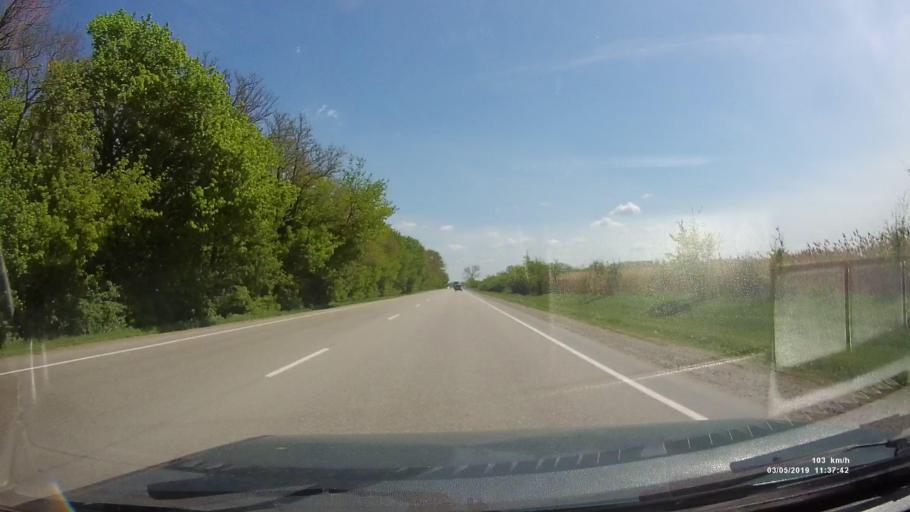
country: RU
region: Rostov
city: Ol'ginskaya
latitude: 47.1312
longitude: 39.9496
